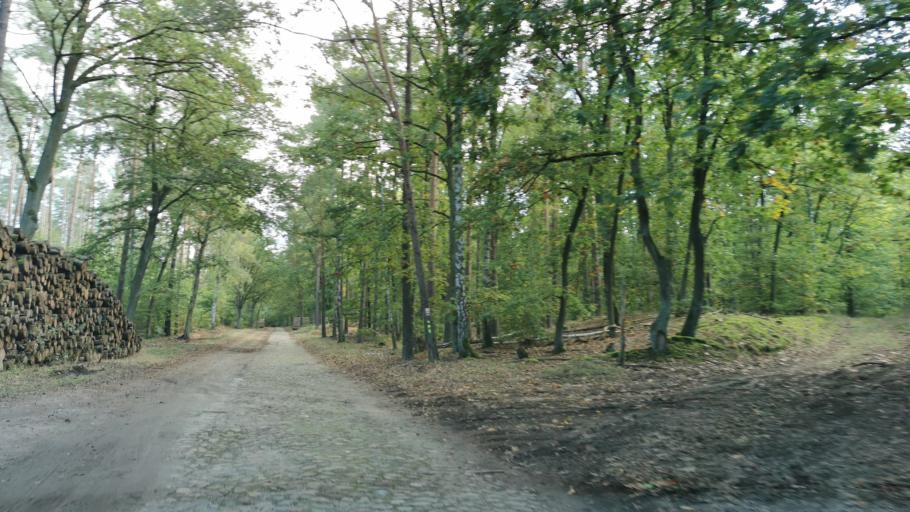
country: DE
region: Brandenburg
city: Michendorf
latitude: 52.3153
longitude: 12.9718
